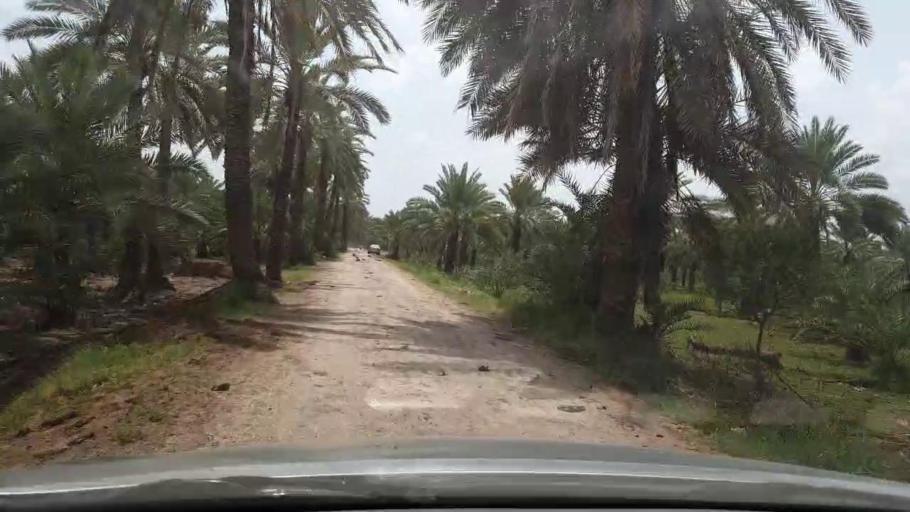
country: PK
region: Sindh
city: Kot Diji
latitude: 27.4052
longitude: 68.7554
